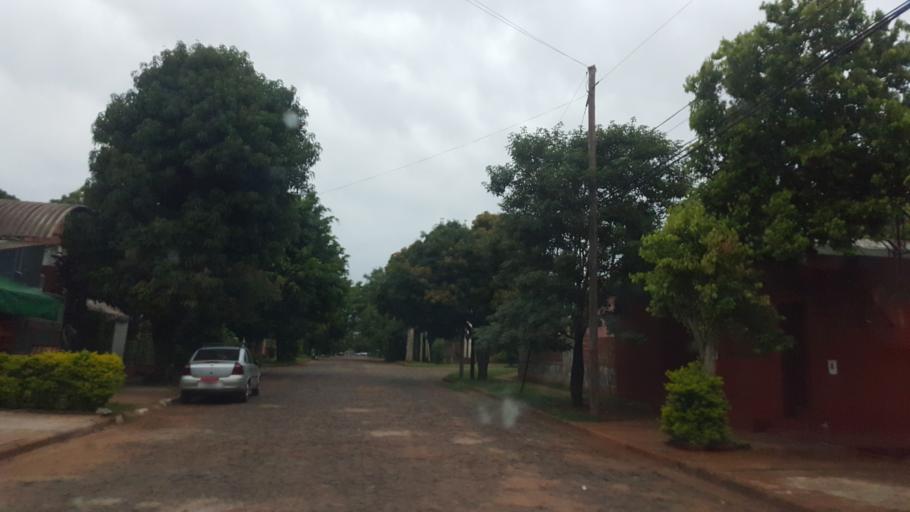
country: AR
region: Misiones
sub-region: Departamento de Capital
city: Posadas
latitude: -27.3728
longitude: -55.9230
